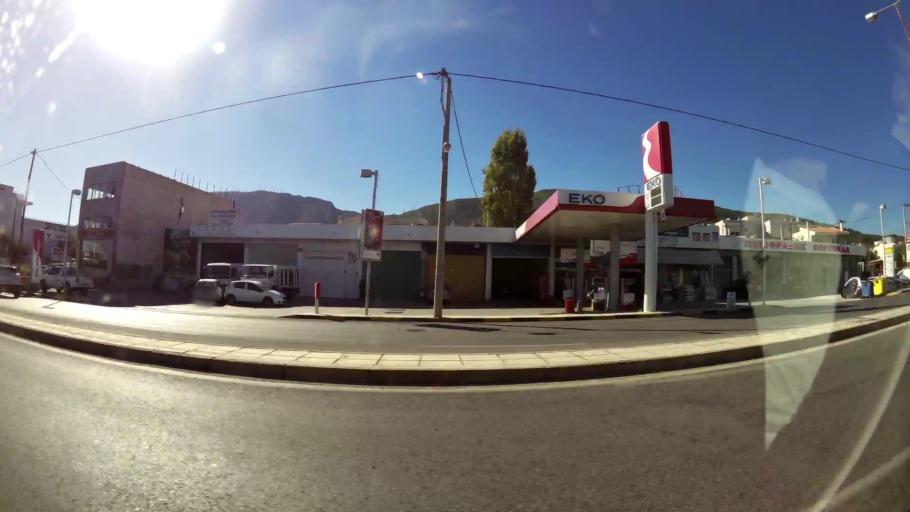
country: GR
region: Attica
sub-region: Nomarchia Anatolikis Attikis
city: Leondarion
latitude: 37.9820
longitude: 23.8518
